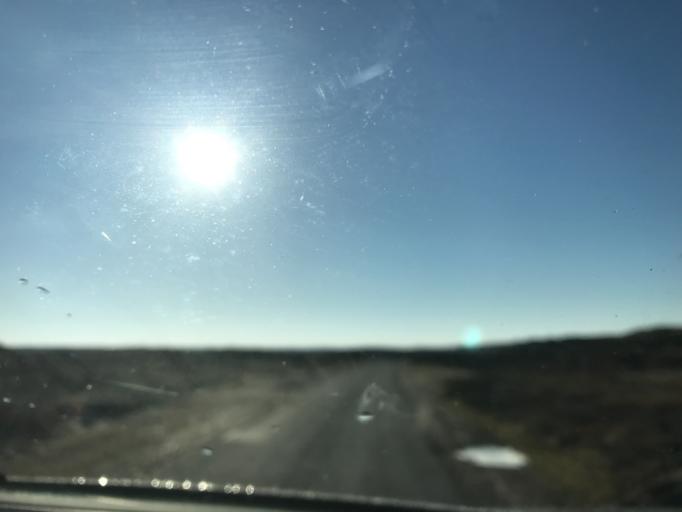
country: DK
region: Central Jutland
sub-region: Ringkobing-Skjern Kommune
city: Hvide Sande
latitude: 55.8129
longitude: 8.1773
